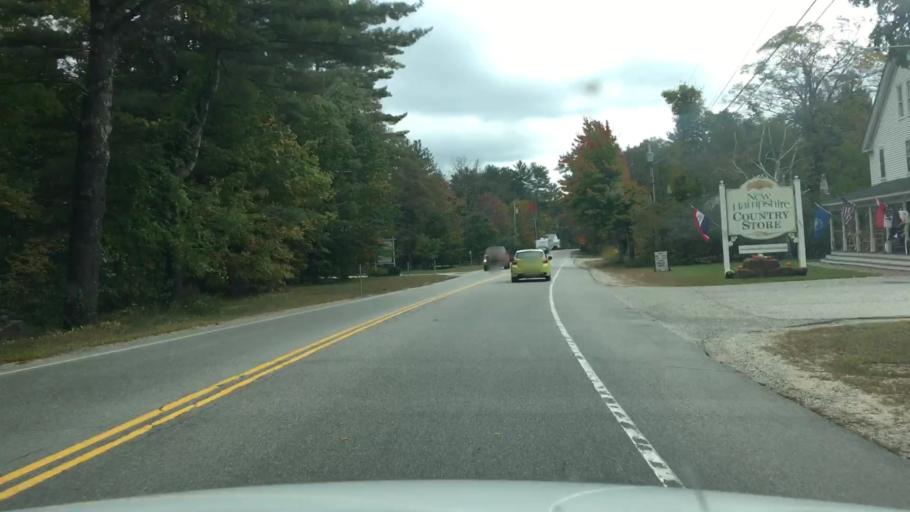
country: US
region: New Hampshire
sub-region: Carroll County
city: Tamworth
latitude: 43.8831
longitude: -71.2247
